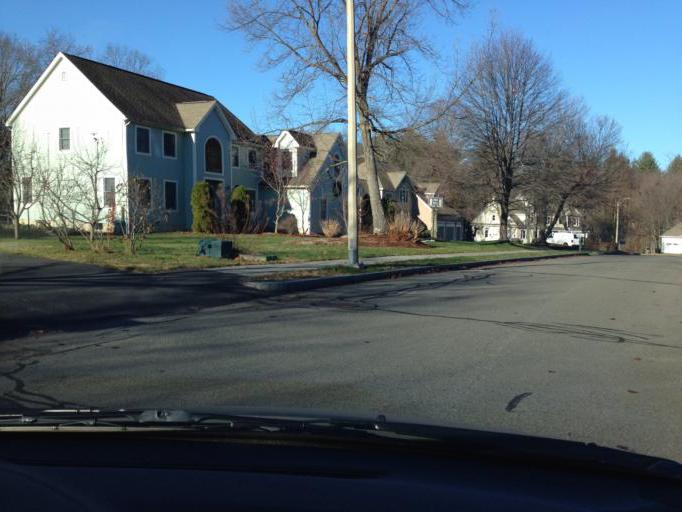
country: US
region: Massachusetts
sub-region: Middlesex County
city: Bedford
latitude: 42.5178
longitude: -71.2754
